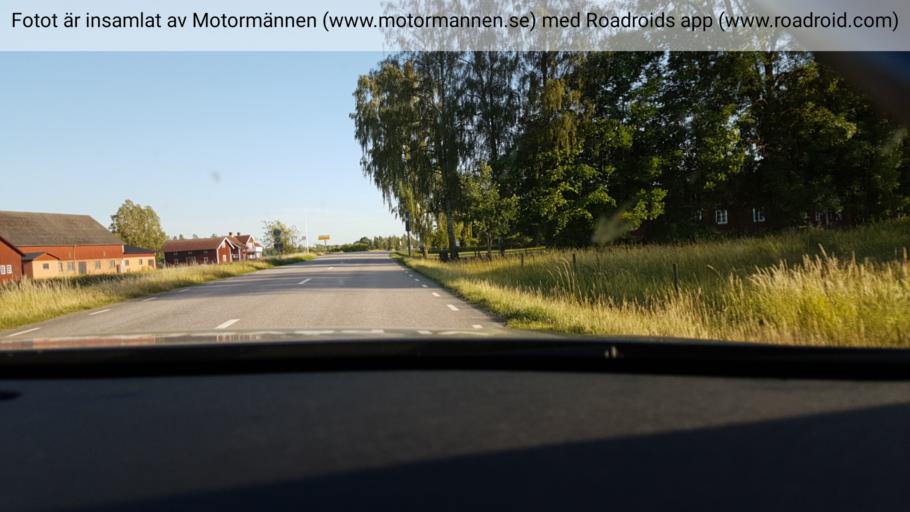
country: SE
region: Vaestra Goetaland
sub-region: Skovde Kommun
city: Stopen
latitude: 58.5510
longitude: 14.0031
